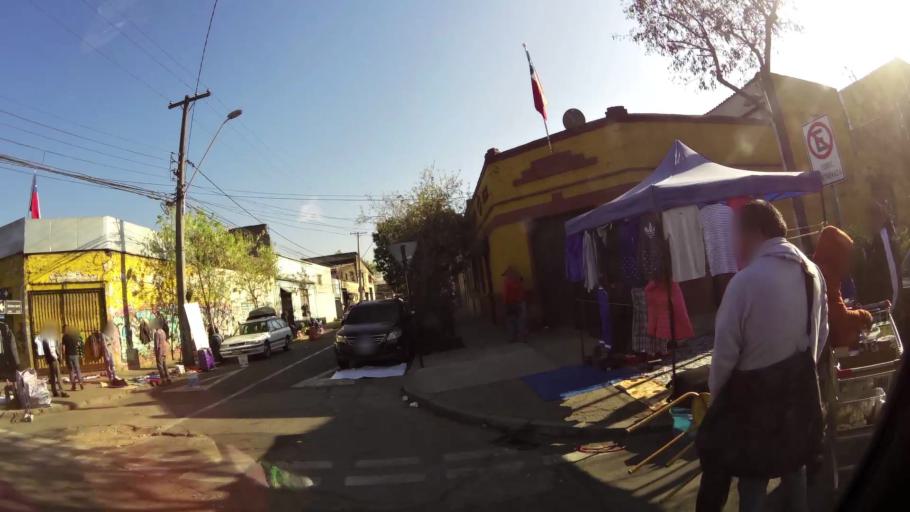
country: CL
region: Santiago Metropolitan
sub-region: Provincia de Santiago
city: Santiago
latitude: -33.4735
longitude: -70.6384
